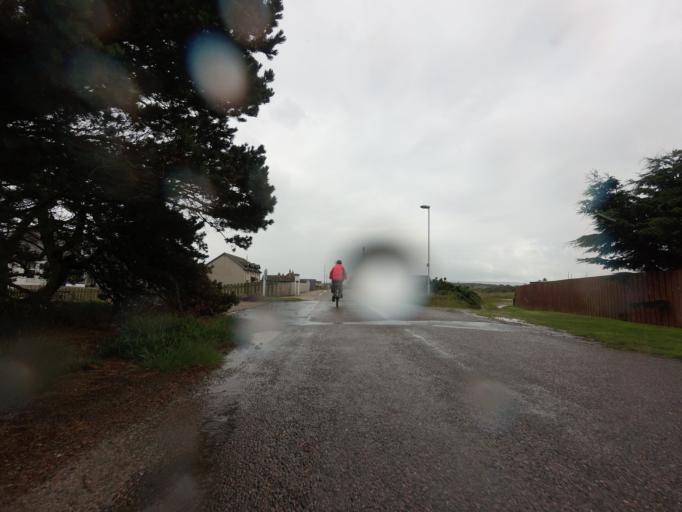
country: GB
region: Scotland
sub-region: Moray
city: Fochabers
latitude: 57.6726
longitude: -3.0867
